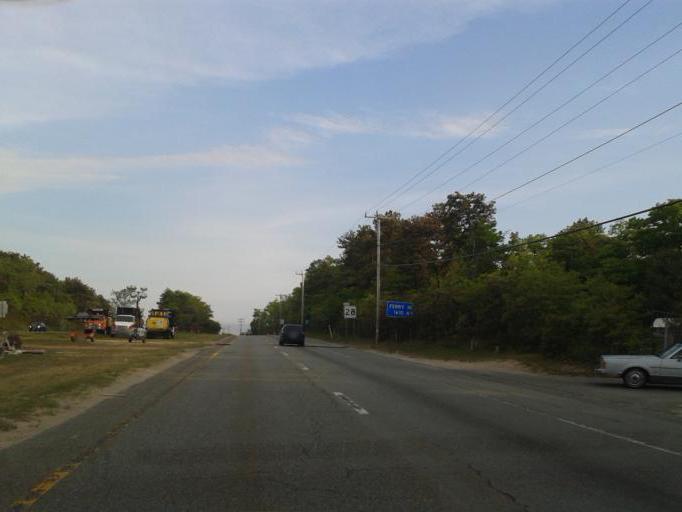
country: US
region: Massachusetts
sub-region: Barnstable County
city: Bourne
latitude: 41.7254
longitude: -70.5846
